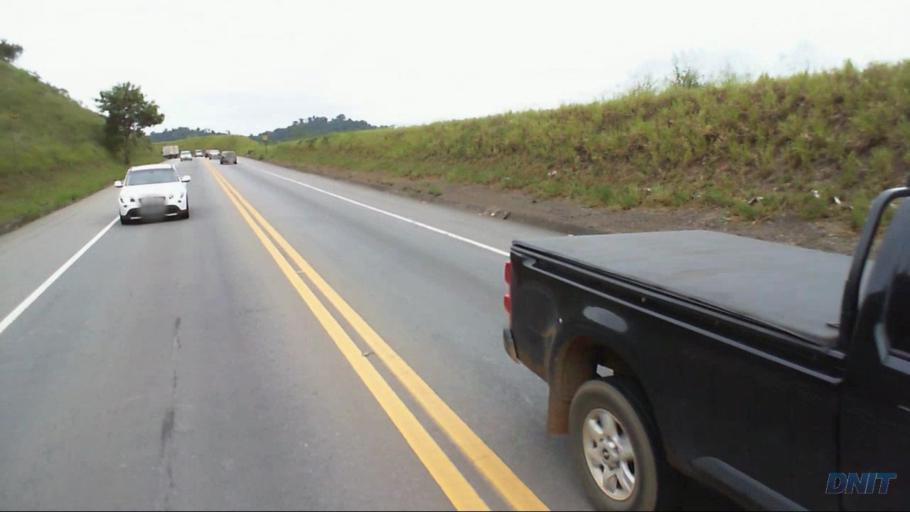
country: BR
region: Minas Gerais
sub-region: Coronel Fabriciano
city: Coronel Fabriciano
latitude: -19.5312
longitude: -42.5827
